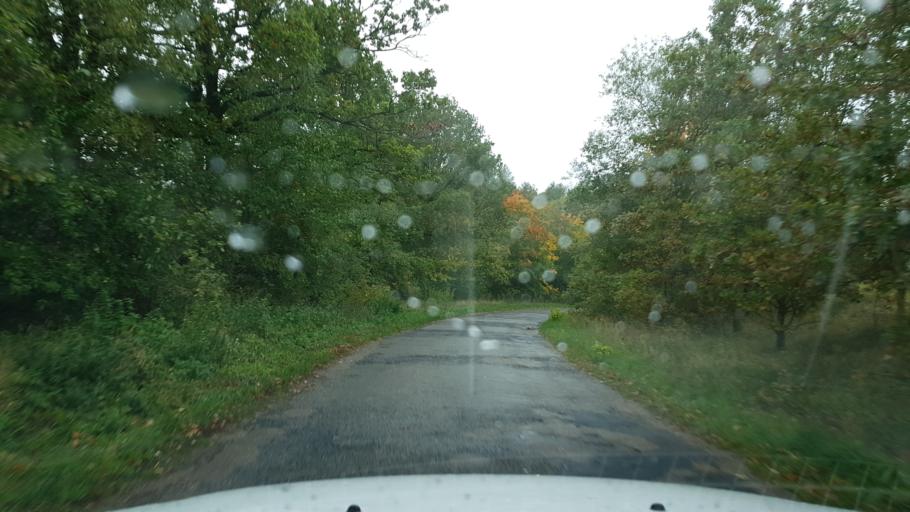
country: PL
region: West Pomeranian Voivodeship
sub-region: Powiat mysliborski
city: Barlinek
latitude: 53.0374
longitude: 15.2389
